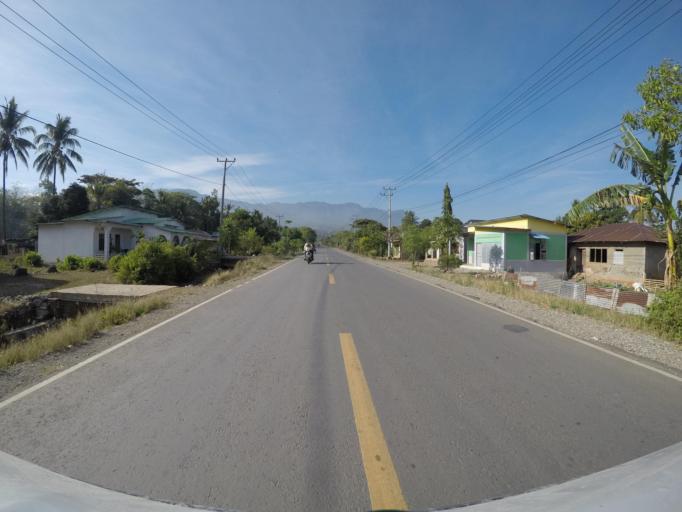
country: TL
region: Bobonaro
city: Maliana
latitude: -8.9798
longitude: 125.2206
